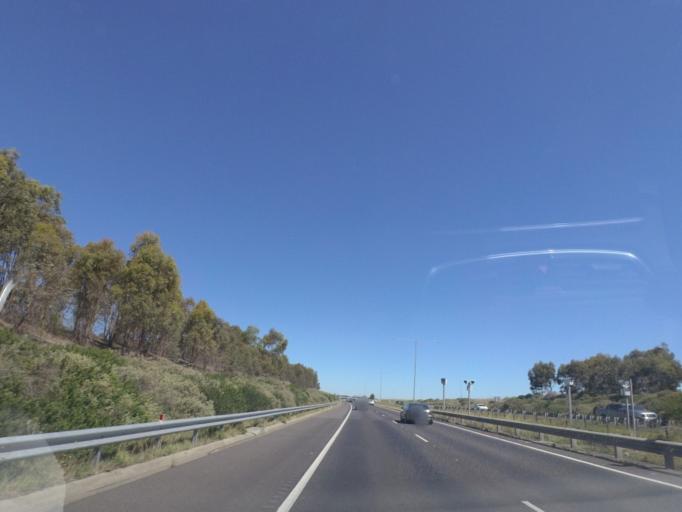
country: AU
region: Victoria
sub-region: Hume
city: Craigieburn
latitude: -37.5841
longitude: 144.9443
